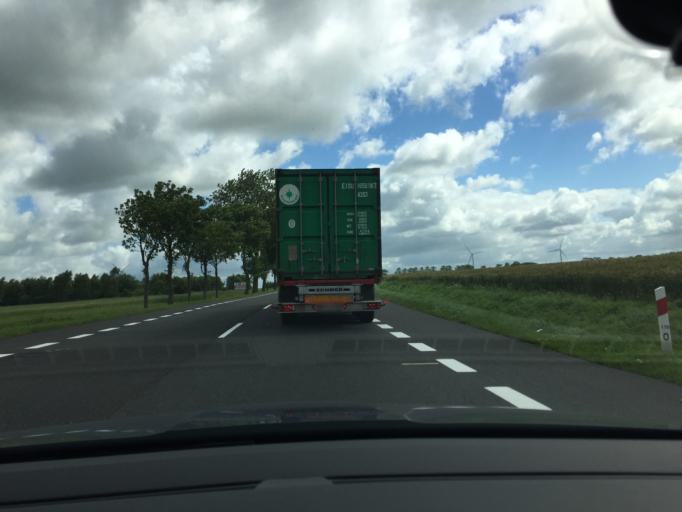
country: PL
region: West Pomeranian Voivodeship
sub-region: Powiat slawienski
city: Darlowo
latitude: 54.3150
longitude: 16.5247
